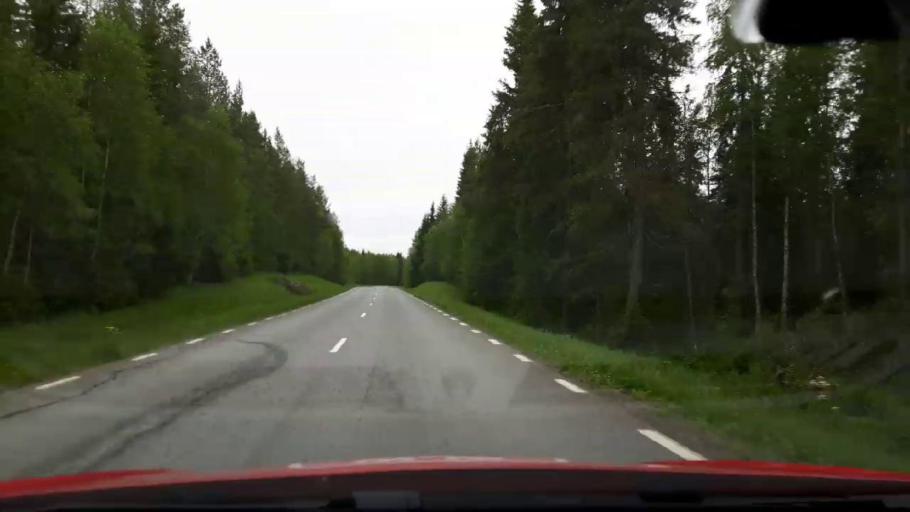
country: SE
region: Jaemtland
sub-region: Stroemsunds Kommun
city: Stroemsund
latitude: 63.4695
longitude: 15.4519
